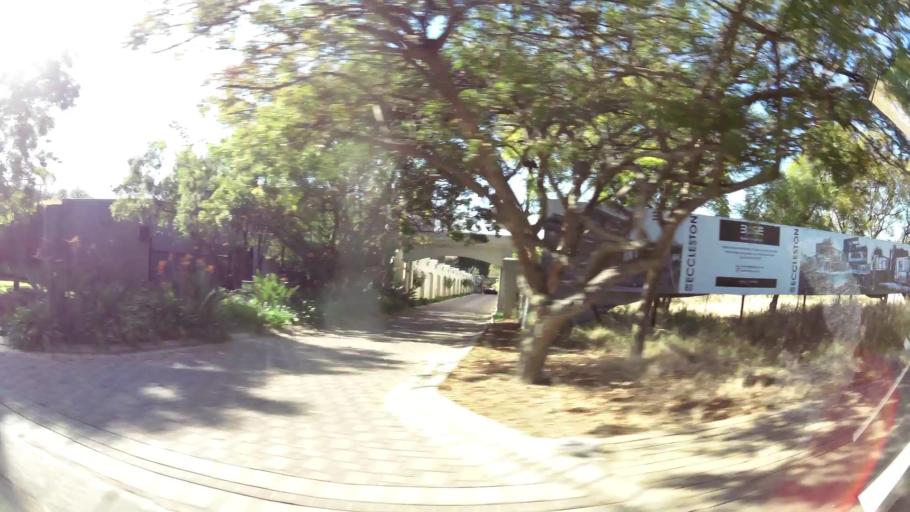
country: ZA
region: Gauteng
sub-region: City of Johannesburg Metropolitan Municipality
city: Midrand
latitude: -26.0550
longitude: 28.0327
